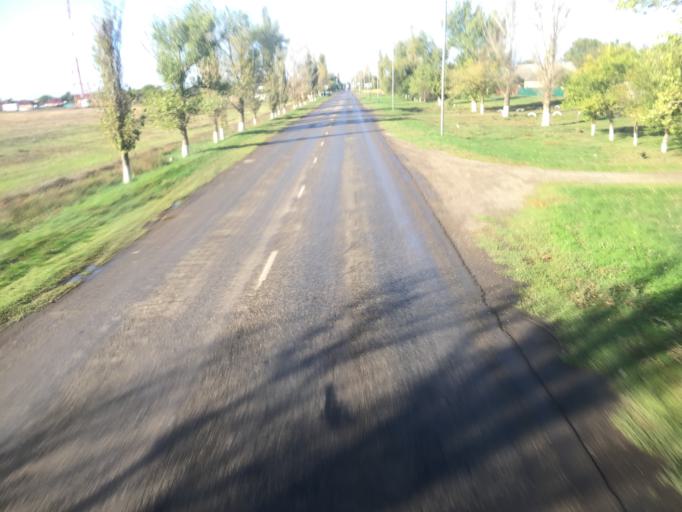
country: RU
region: Rostov
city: Peschanokopskoye
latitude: 46.1936
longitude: 41.1033
